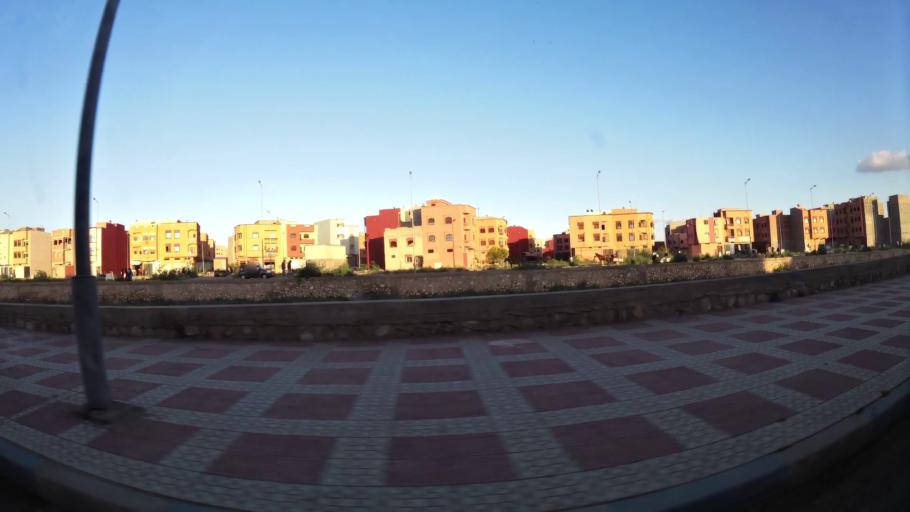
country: MA
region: Marrakech-Tensift-Al Haouz
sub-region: Kelaa-Des-Sraghna
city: Sidi Abdallah
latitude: 32.2372
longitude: -7.9504
